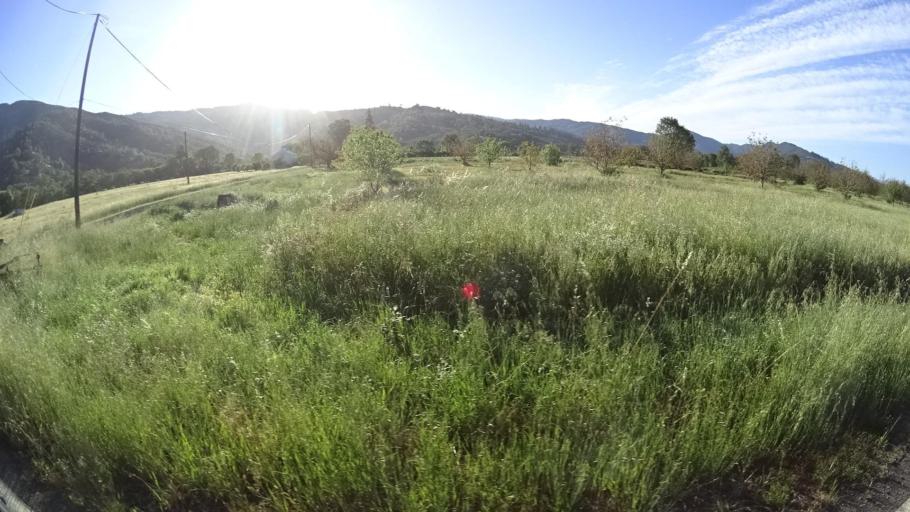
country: US
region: California
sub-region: Lake County
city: Upper Lake
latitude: 39.1908
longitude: -122.9004
